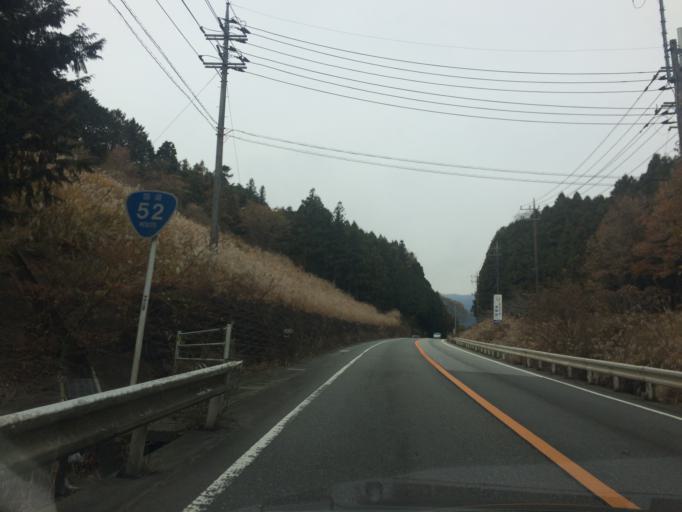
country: JP
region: Shizuoka
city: Fujinomiya
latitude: 35.2699
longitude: 138.4554
